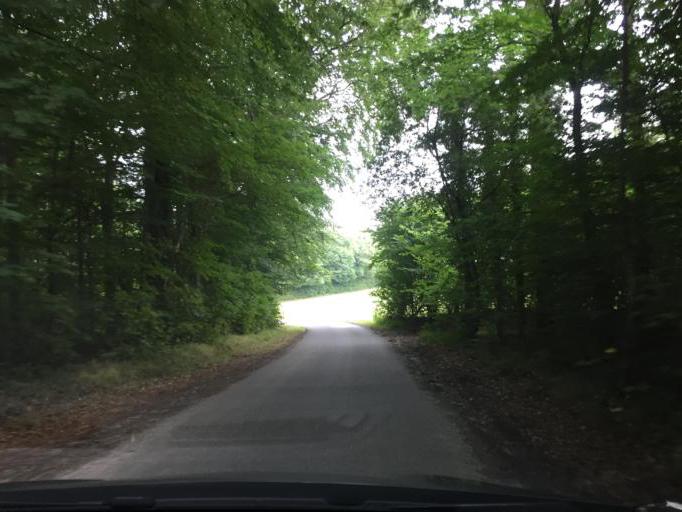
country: DK
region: South Denmark
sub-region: Assens Kommune
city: Harby
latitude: 55.1985
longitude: 10.0369
